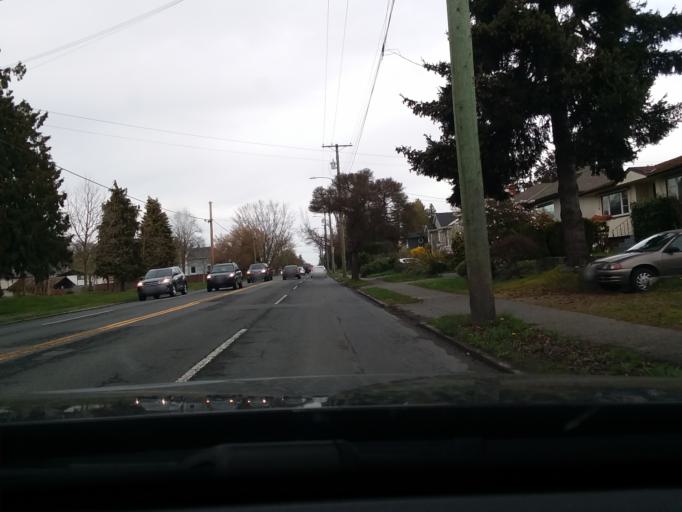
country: CA
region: British Columbia
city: Oak Bay
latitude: 48.4513
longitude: -123.3331
